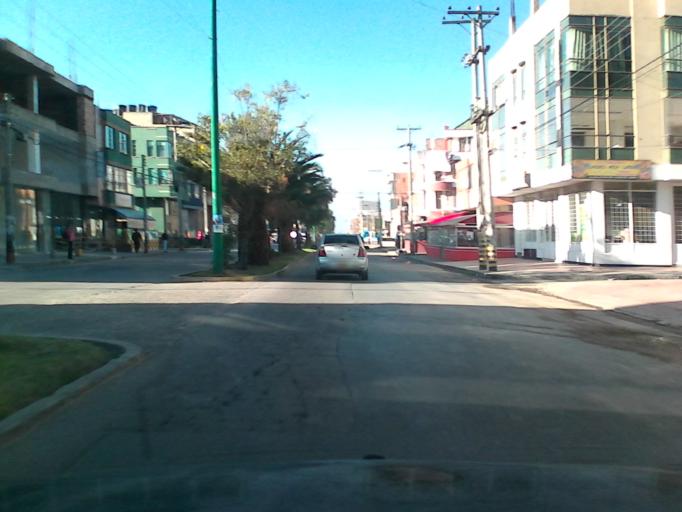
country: CO
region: Boyaca
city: Duitama
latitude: 5.8166
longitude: -73.0299
